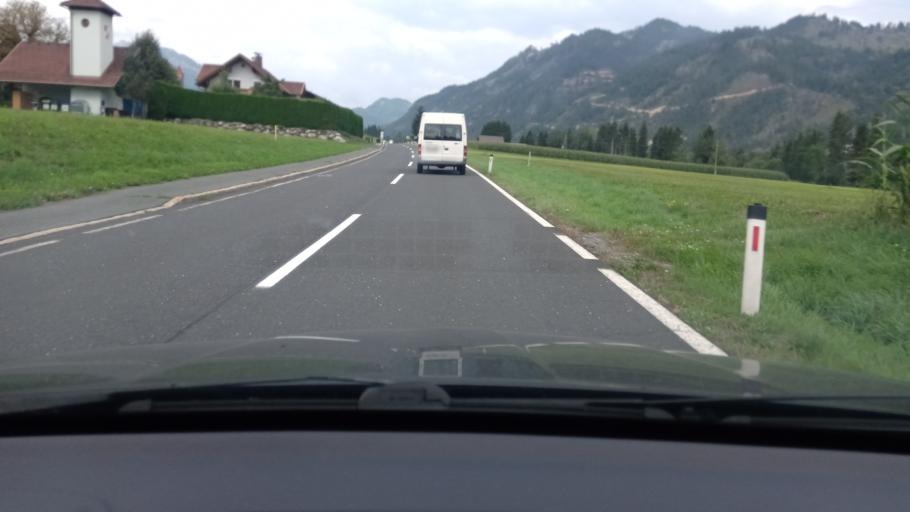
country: AT
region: Carinthia
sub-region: Politischer Bezirk Hermagor
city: Hermagor
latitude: 46.6613
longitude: 13.3115
